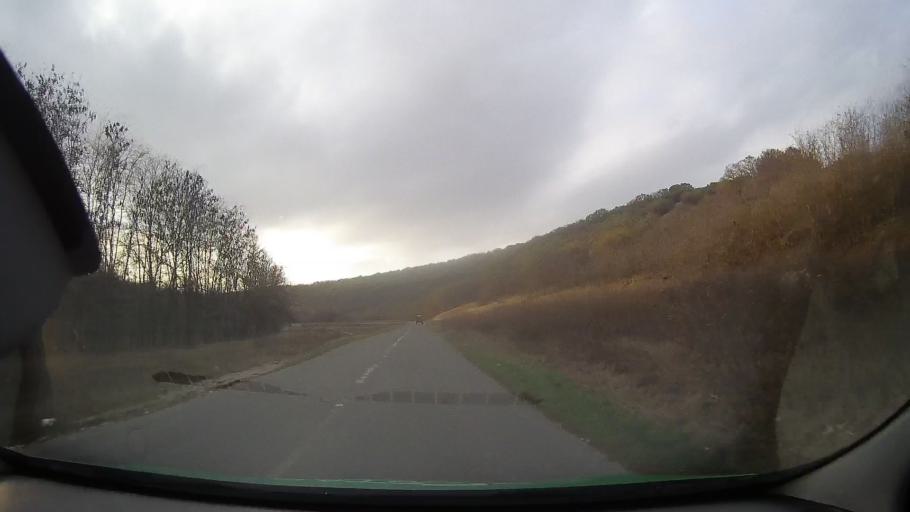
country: RO
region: Constanta
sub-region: Comuna Adamclisi
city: Adamclisi
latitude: 44.0395
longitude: 27.9471
